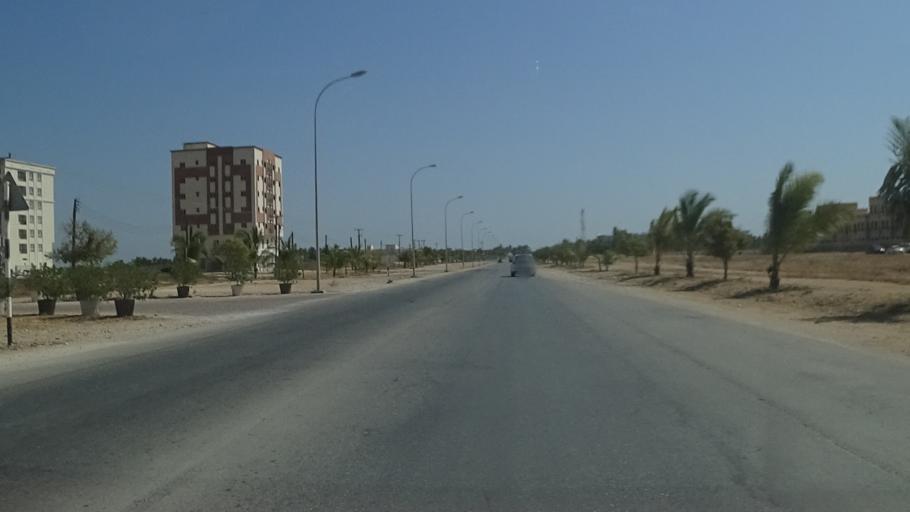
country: OM
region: Zufar
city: Salalah
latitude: 17.0467
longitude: 54.1689
